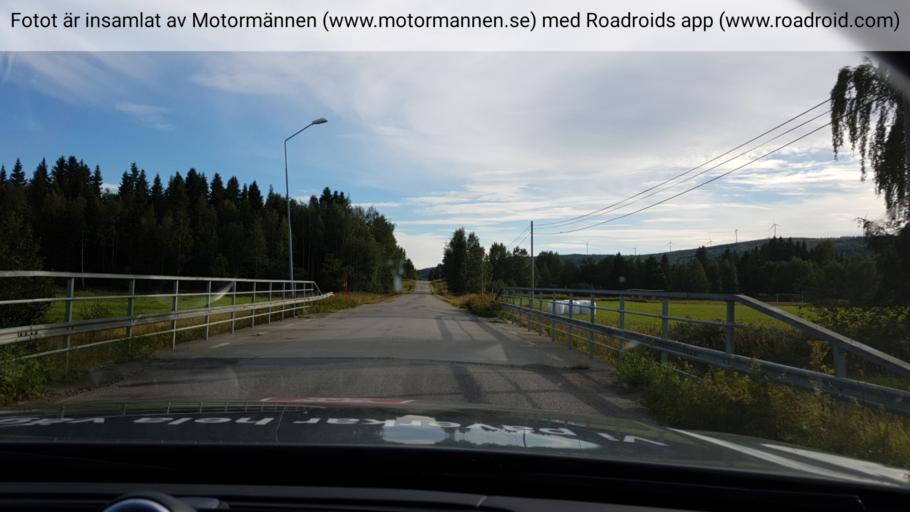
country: SE
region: Jaemtland
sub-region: Stroemsunds Kommun
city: Stroemsund
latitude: 64.0693
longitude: 15.8228
